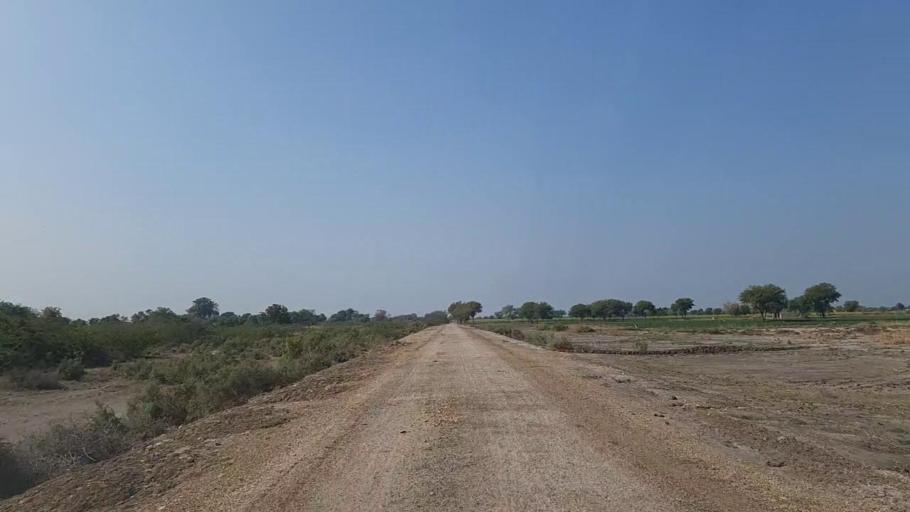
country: PK
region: Sindh
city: Nawabshah
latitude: 26.2948
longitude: 68.4785
